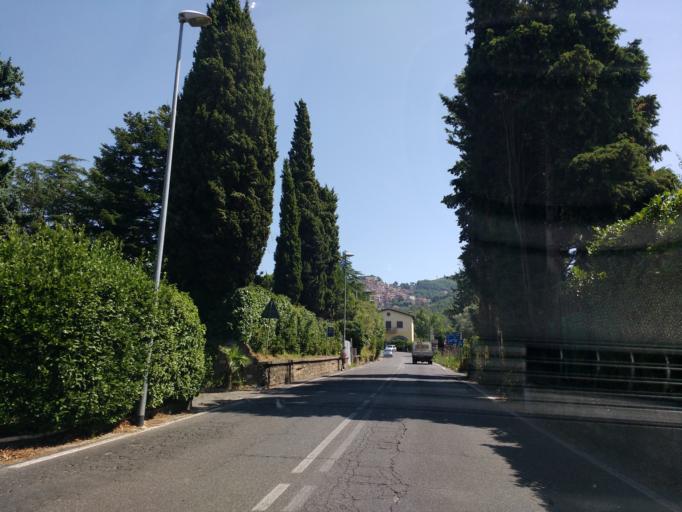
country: IT
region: Latium
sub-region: Citta metropolitana di Roma Capitale
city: Rocca di Papa
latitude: 41.7732
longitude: 12.6996
